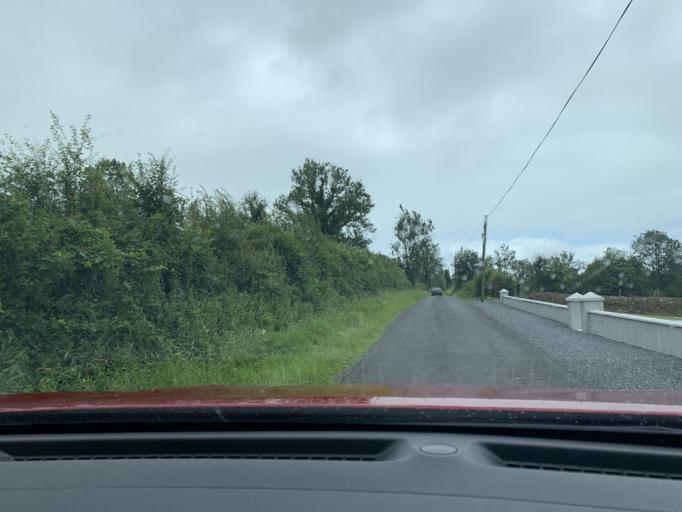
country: IE
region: Connaught
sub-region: County Leitrim
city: Carrick-on-Shannon
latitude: 53.8713
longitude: -8.1479
